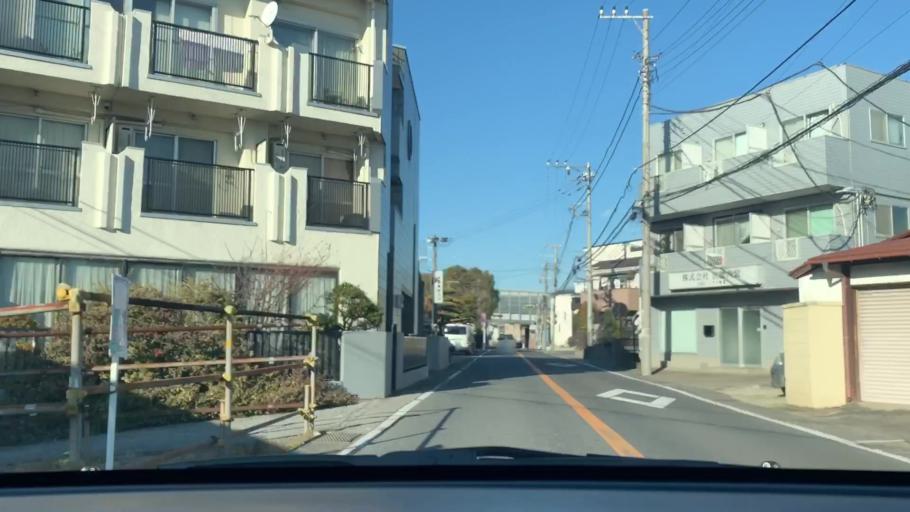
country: JP
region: Tokyo
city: Urayasu
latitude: 35.7093
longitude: 139.9189
